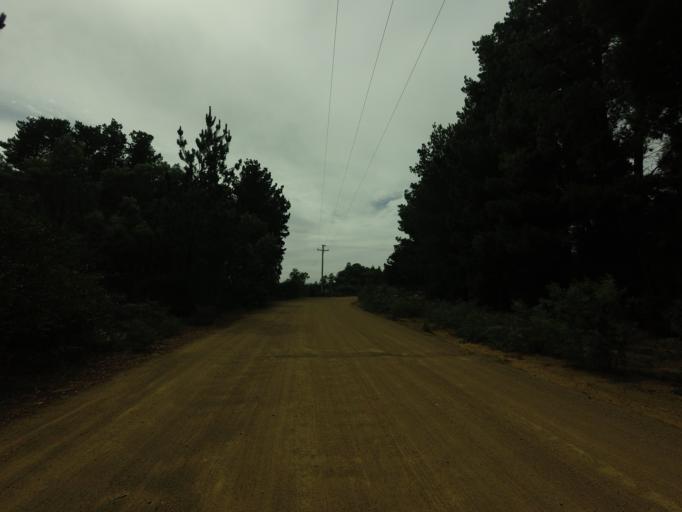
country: AU
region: Tasmania
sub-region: Clarence
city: Seven Mile Beach
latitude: -42.8453
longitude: 147.5110
